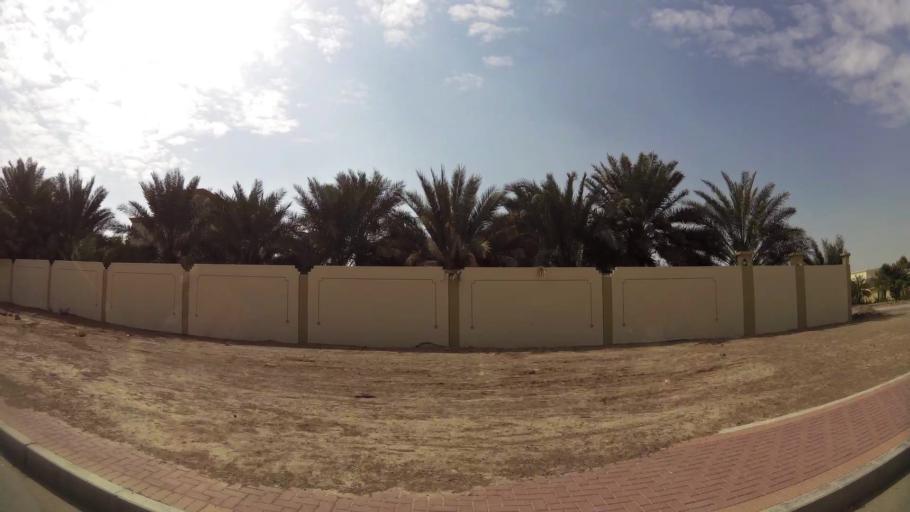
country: AE
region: Abu Dhabi
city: Al Ain
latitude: 24.0960
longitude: 55.9034
